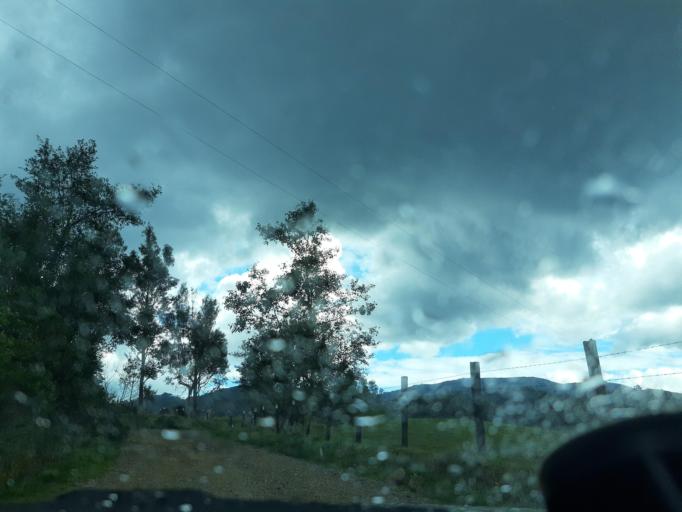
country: CO
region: Boyaca
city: Raquira
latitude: 5.4918
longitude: -73.7004
